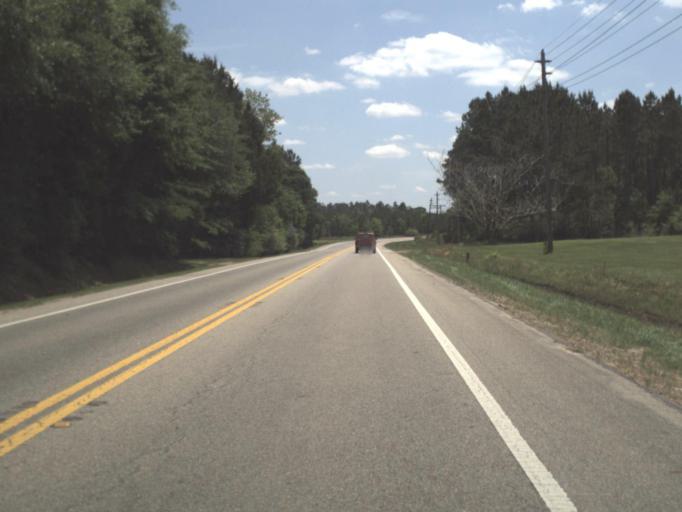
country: US
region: Florida
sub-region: Calhoun County
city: Blountstown
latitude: 30.4654
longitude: -85.0725
